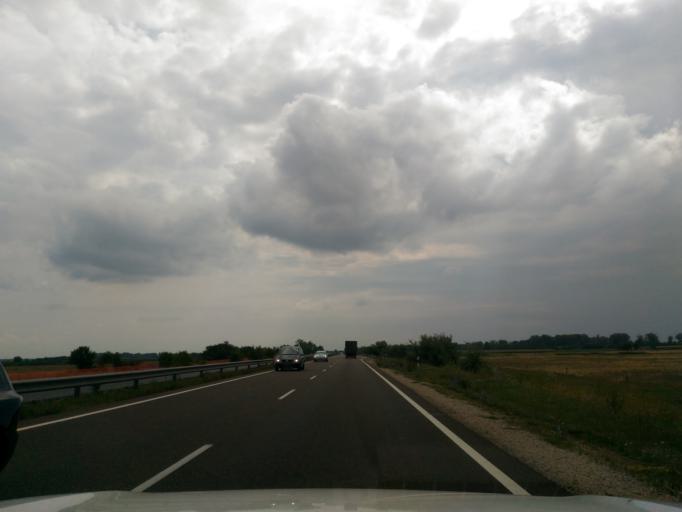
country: HU
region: Pest
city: Cegled
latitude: 47.1906
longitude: 19.8726
